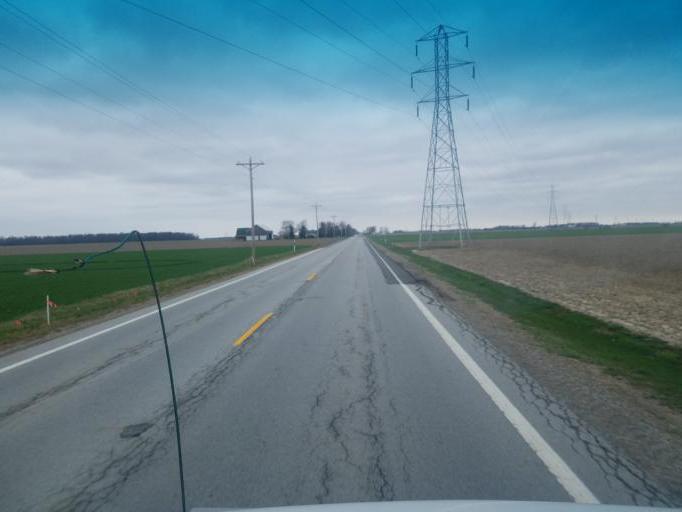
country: US
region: Ohio
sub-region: Allen County
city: Delphos
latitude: 40.9324
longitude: -84.3832
